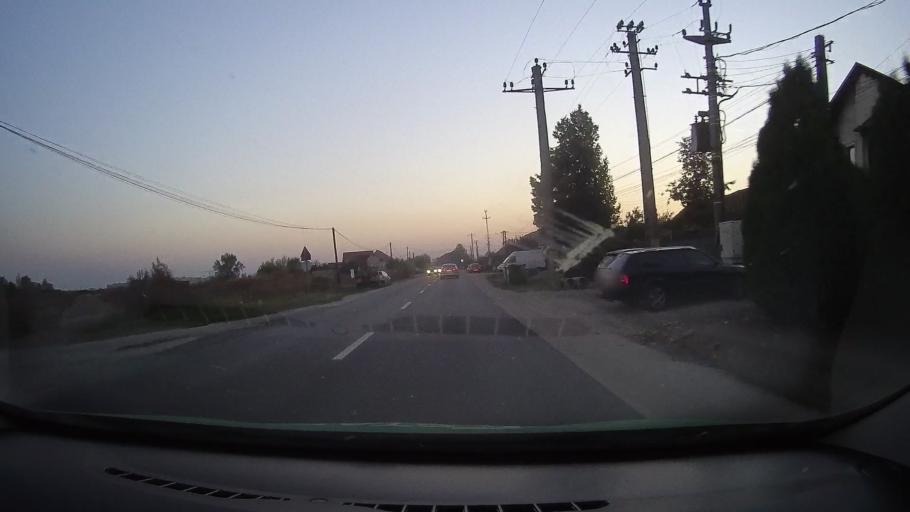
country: RO
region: Arad
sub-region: Comuna Zimandu Nou
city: Zimandu Nou
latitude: 46.2788
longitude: 21.3953
